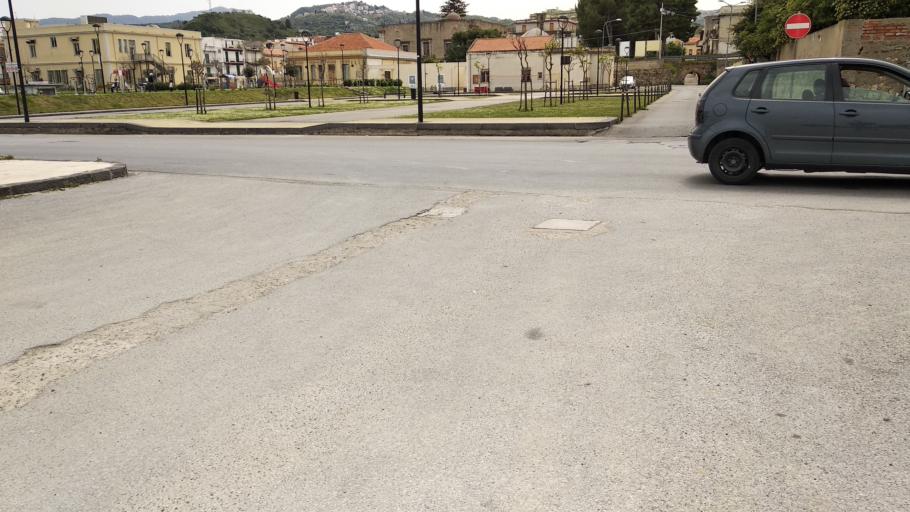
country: IT
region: Sicily
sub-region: Messina
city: Venetico Marina
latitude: 38.2230
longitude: 15.3735
